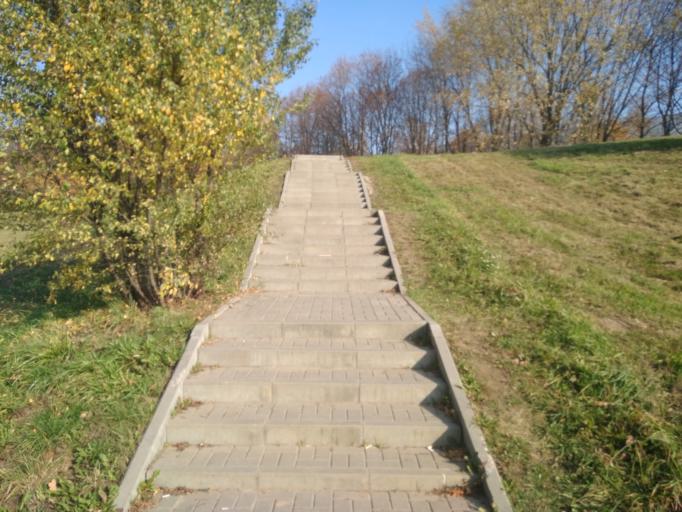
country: BY
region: Minsk
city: Novoye Medvezhino
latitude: 53.9118
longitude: 27.4715
